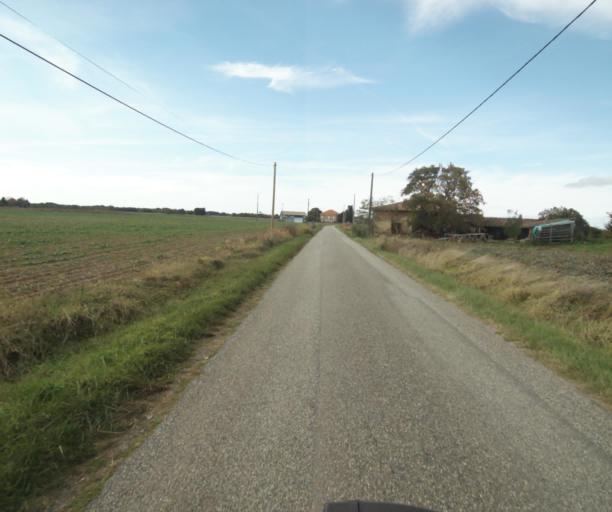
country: FR
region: Midi-Pyrenees
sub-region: Departement du Tarn-et-Garonne
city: Saint-Porquier
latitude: 43.9506
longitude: 1.1568
